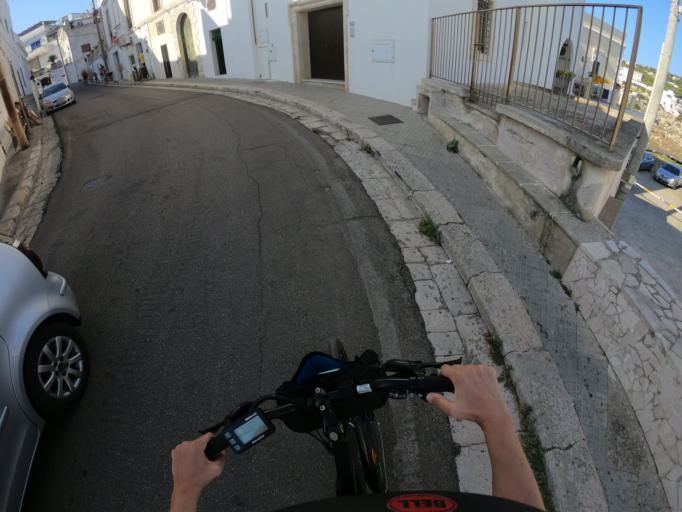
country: IT
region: Apulia
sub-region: Provincia di Lecce
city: Leuca
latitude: 39.7976
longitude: 18.3601
